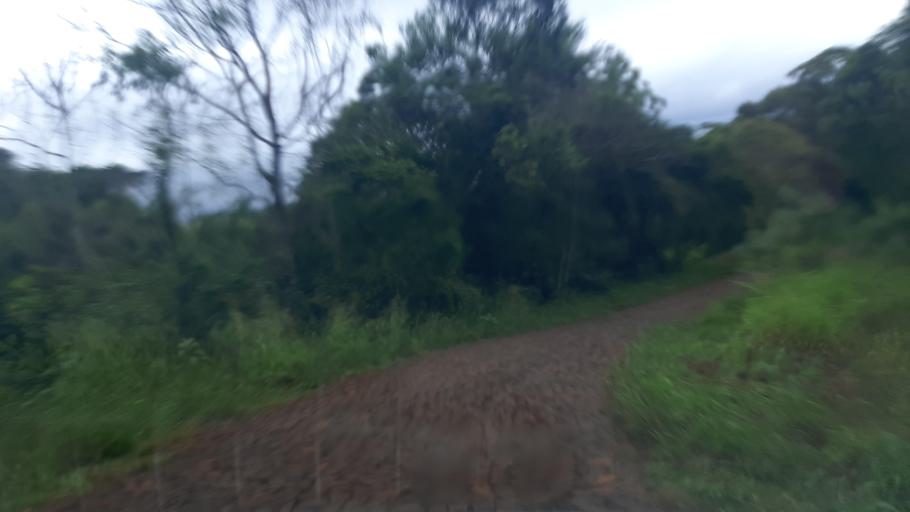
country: BR
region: Parana
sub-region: Ampere
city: Ampere
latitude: -26.0390
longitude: -53.5127
